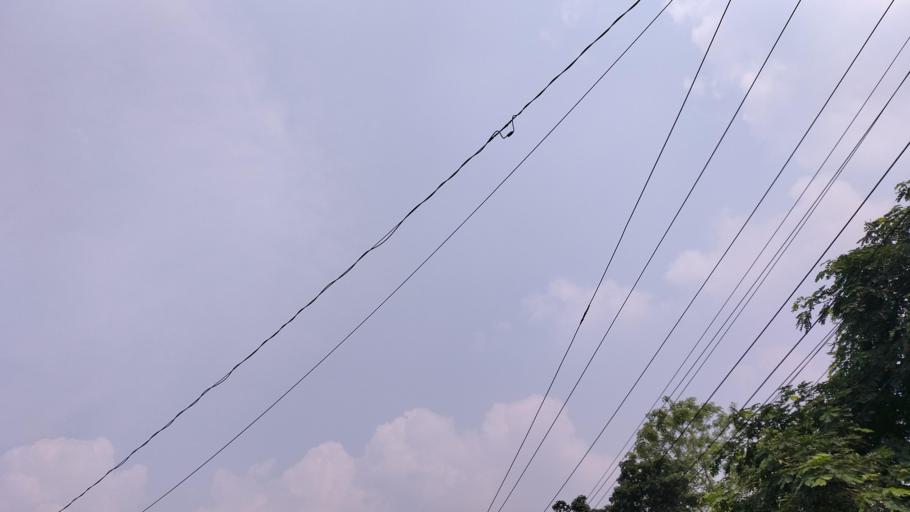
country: BD
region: Dhaka
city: Azimpur
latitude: 23.6952
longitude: 90.2994
